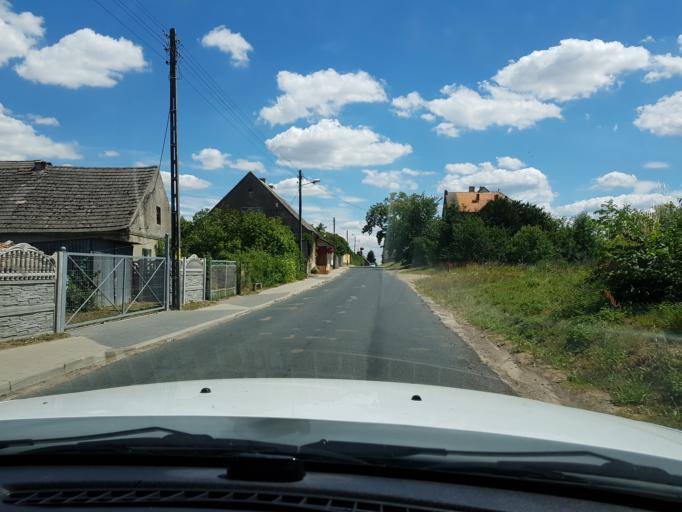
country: PL
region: West Pomeranian Voivodeship
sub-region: Powiat mysliborski
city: Nowogrodek Pomorski
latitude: 52.9088
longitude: 14.9604
